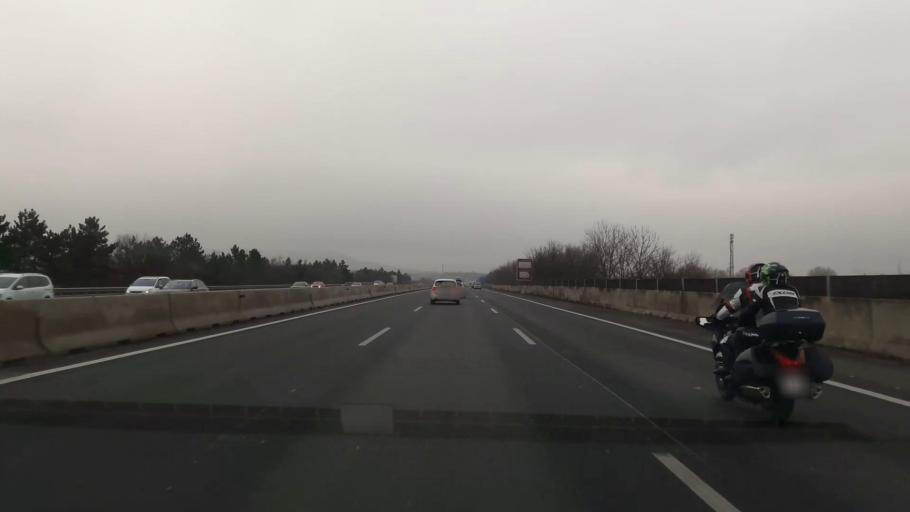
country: AT
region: Lower Austria
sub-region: Politischer Bezirk Baden
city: Leobersdorf
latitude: 47.9178
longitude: 16.2085
